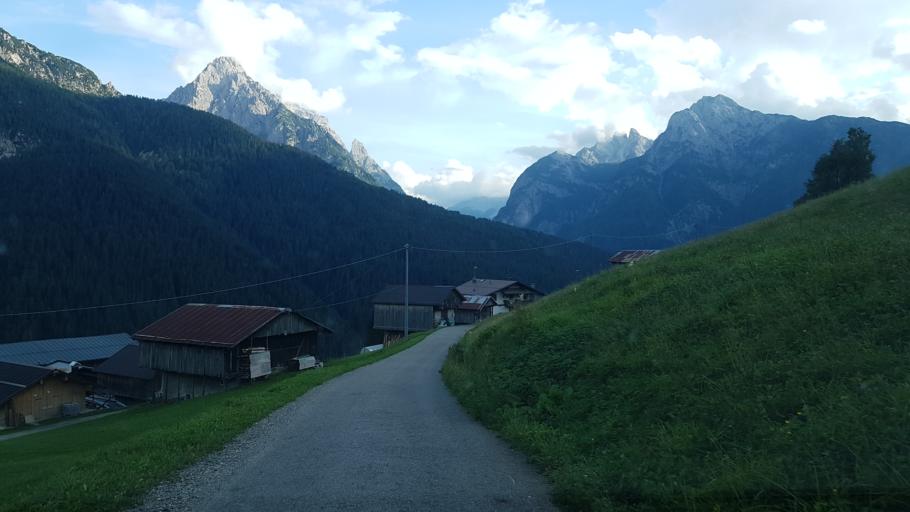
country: IT
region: Veneto
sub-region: Provincia di Belluno
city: San Pietro di Cadore
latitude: 46.5814
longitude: 12.5959
